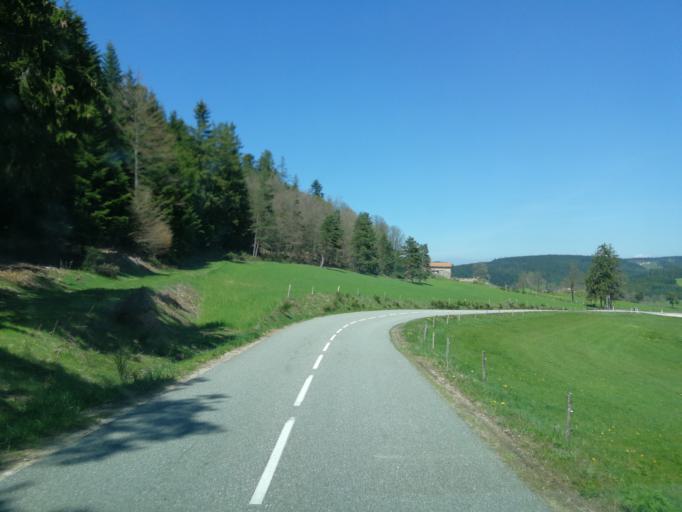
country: FR
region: Rhone-Alpes
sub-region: Departement de la Loire
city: Marlhes
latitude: 45.2901
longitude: 4.3868
